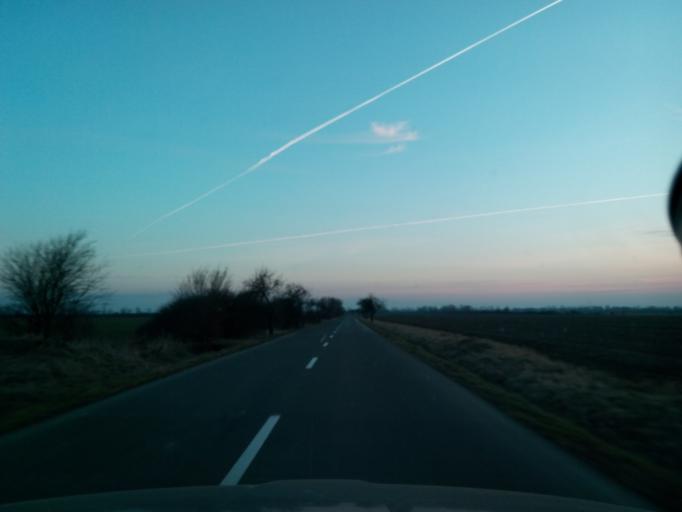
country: SK
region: Kosicky
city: Sobrance
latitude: 48.7773
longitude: 22.1286
